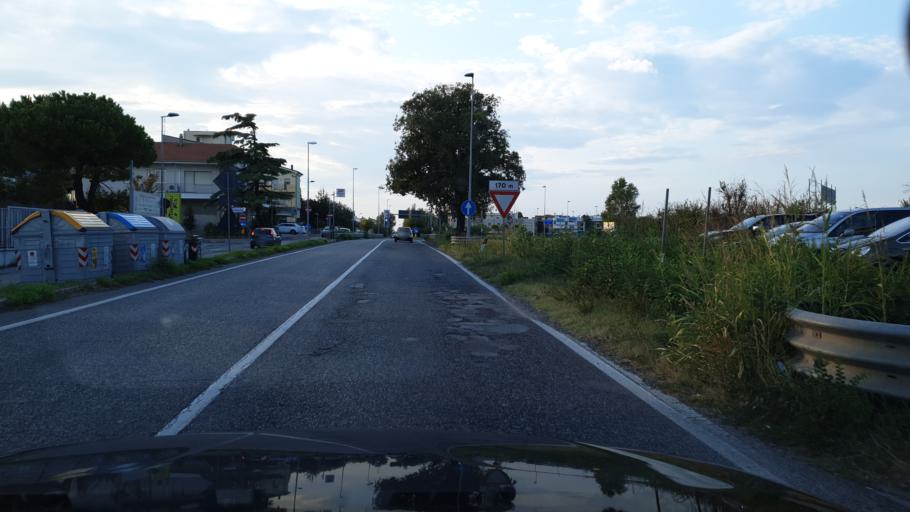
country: IT
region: Emilia-Romagna
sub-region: Provincia di Rimini
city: Rivazzurra
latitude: 44.0302
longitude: 12.6088
